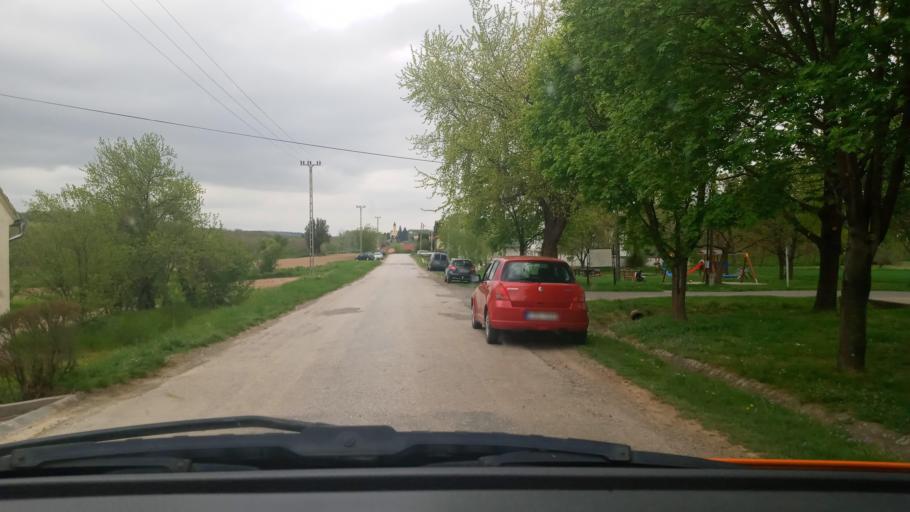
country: HU
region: Baranya
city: Boly
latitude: 45.9965
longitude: 18.5563
